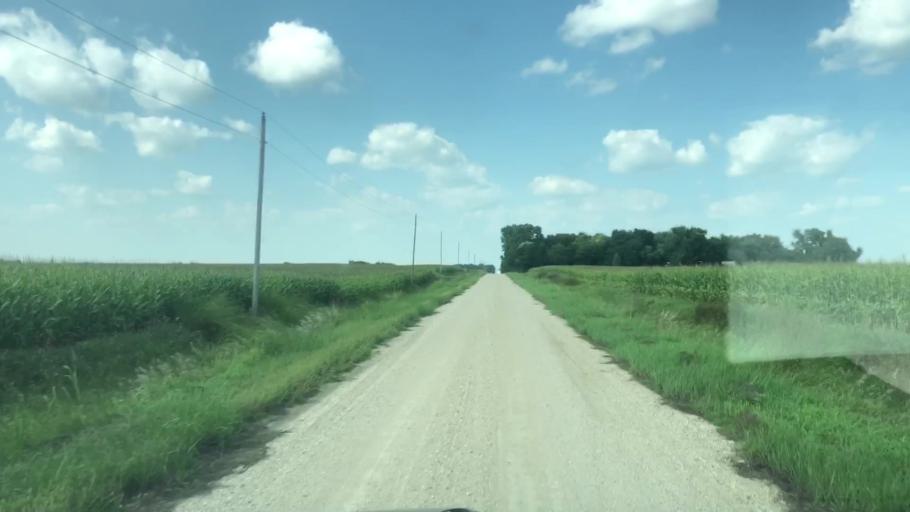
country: US
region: Iowa
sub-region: O'Brien County
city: Sheldon
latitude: 43.1592
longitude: -95.7821
